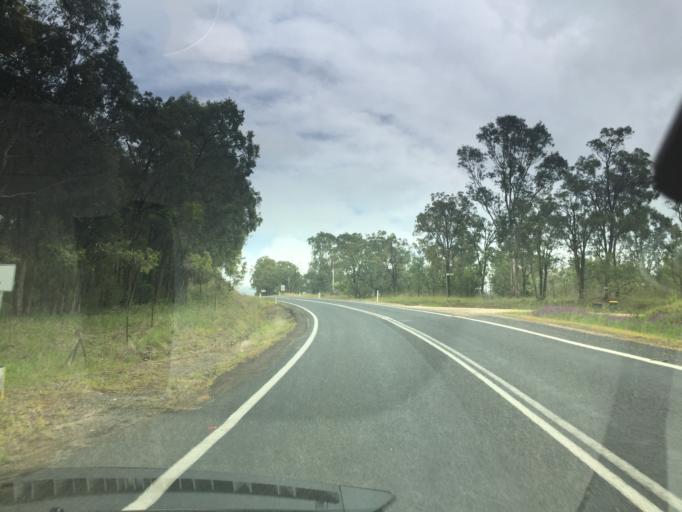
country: AU
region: New South Wales
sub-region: Bega Valley
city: Bega
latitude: -36.6333
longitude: 149.5768
